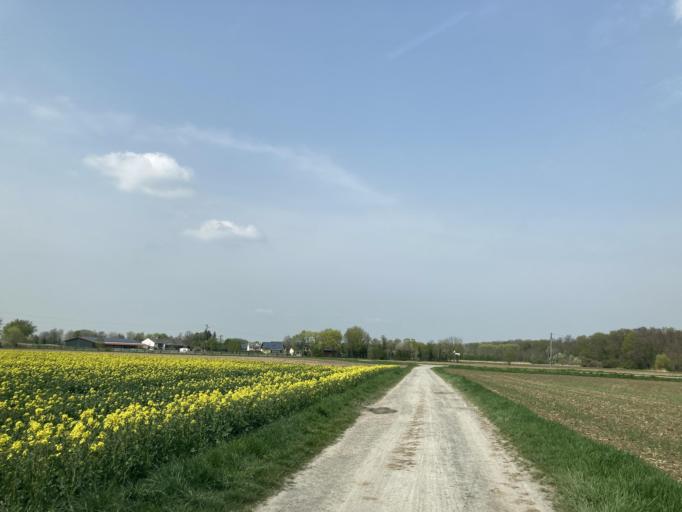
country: DE
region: Baden-Wuerttemberg
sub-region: Karlsruhe Region
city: Kronau
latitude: 49.2316
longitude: 8.6415
